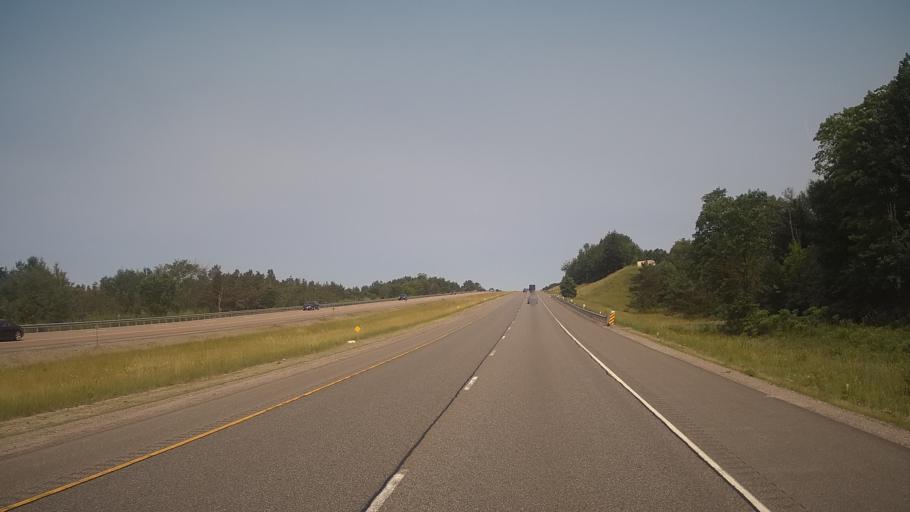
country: CA
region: Ontario
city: Barrie
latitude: 44.4881
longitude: -79.7061
